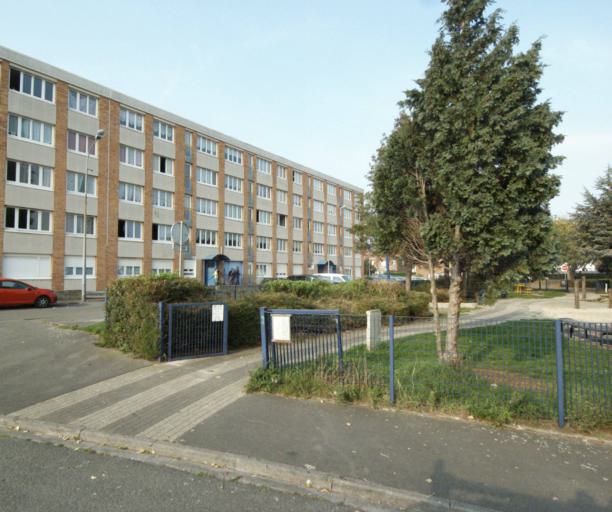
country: FR
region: Nord-Pas-de-Calais
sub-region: Departement du Nord
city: Haubourdin
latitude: 50.5998
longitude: 2.9937
